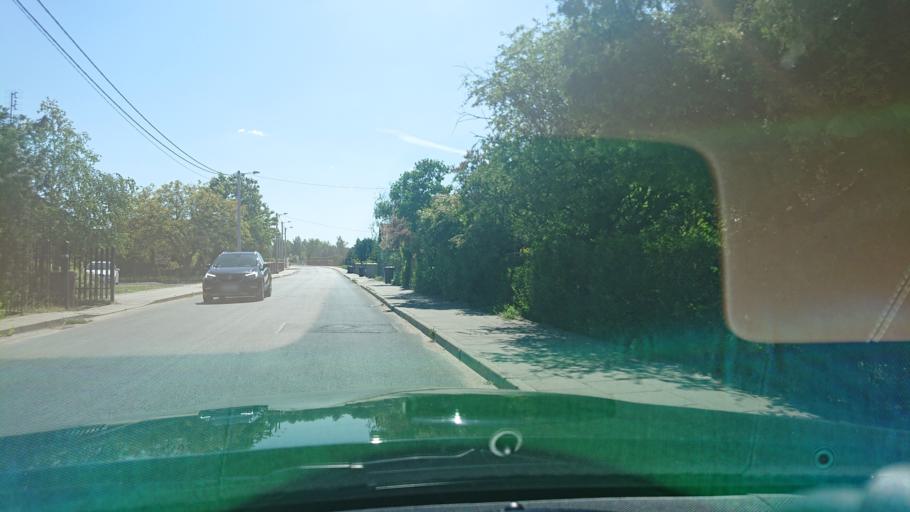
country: PL
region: Greater Poland Voivodeship
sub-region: Powiat gnieznienski
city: Gniezno
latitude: 52.5033
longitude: 17.5864
